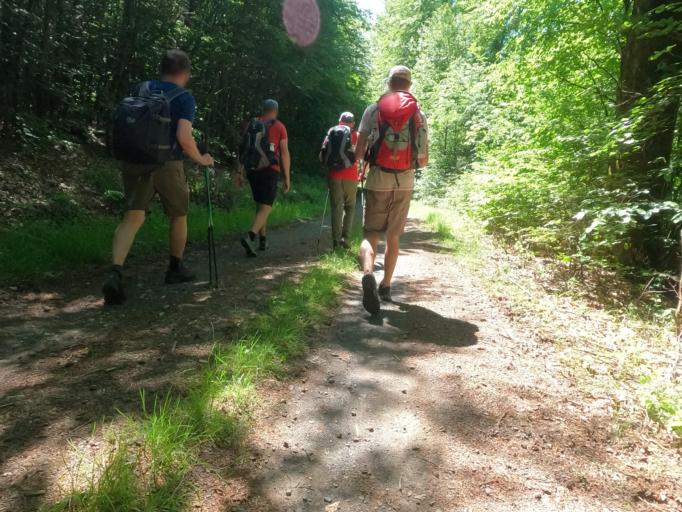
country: DE
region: Rheinland-Pfalz
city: Alpenrod
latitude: 50.6556
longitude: 7.8694
